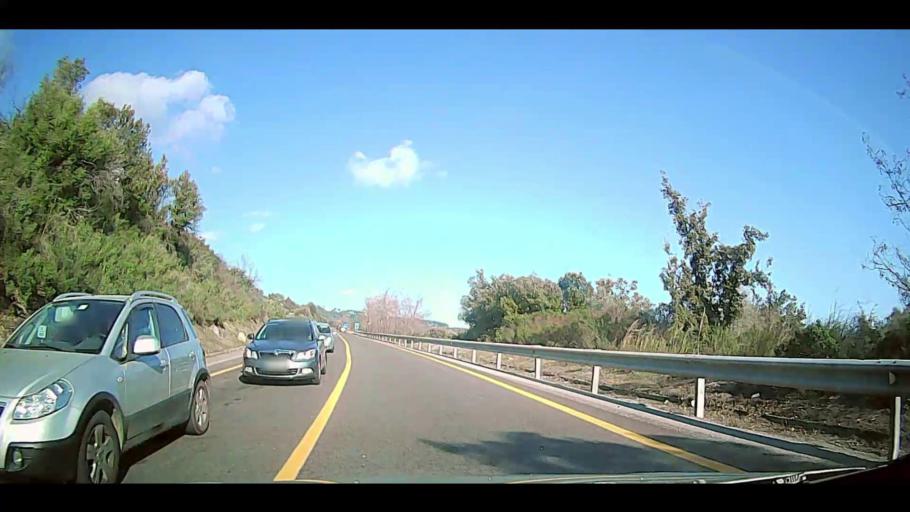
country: IT
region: Calabria
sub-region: Provincia di Crotone
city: Caccuri
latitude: 39.2266
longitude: 16.7958
